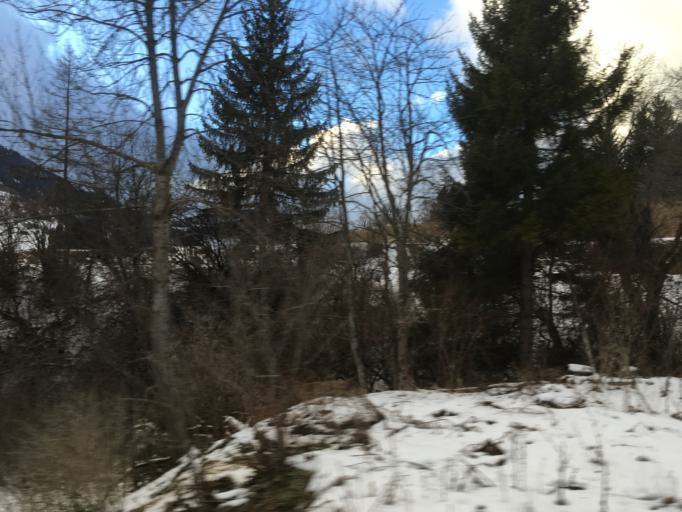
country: CH
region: Grisons
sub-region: Albula District
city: Tiefencastel
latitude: 46.6727
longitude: 9.5735
